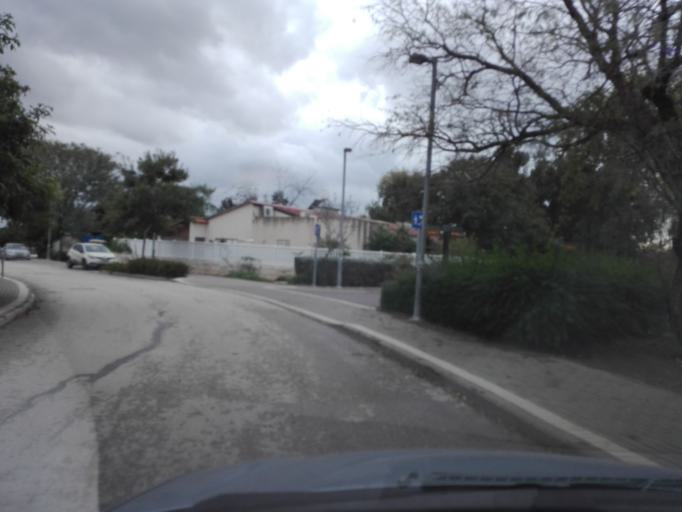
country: IL
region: Northern District
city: El Mazra`a
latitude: 32.9644
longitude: 35.0992
